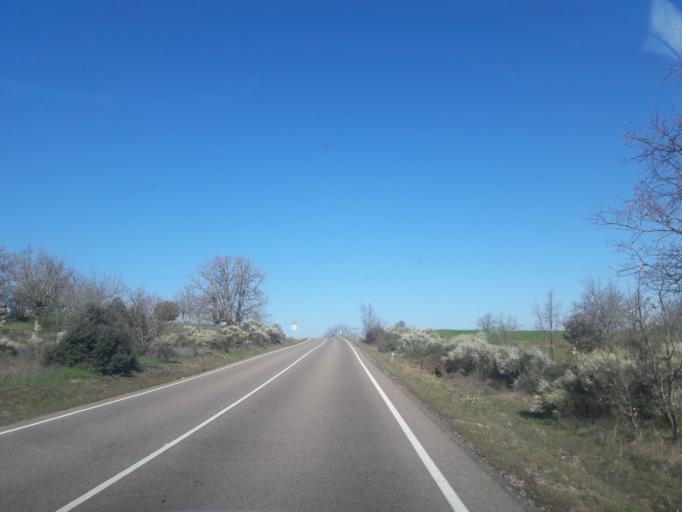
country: ES
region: Castille and Leon
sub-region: Provincia de Salamanca
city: Valderrodrigo
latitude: 41.0749
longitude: -6.5466
